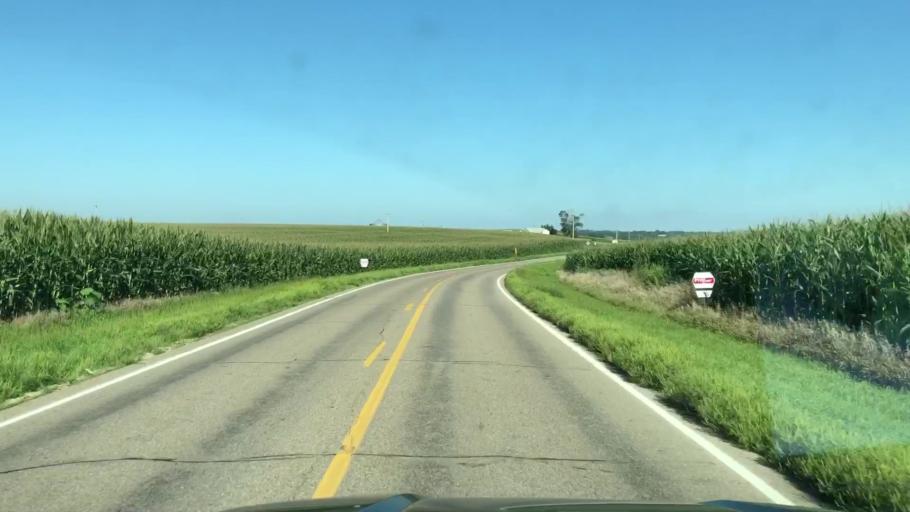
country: US
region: Iowa
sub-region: Woodbury County
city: Sergeant Bluff
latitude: 42.4323
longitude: -96.2893
